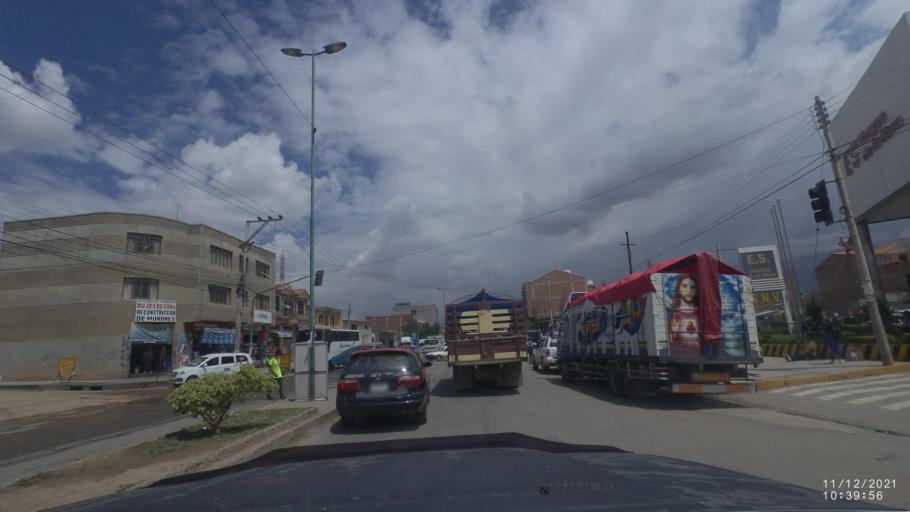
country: BO
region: Cochabamba
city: Cochabamba
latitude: -17.4332
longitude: -66.1266
